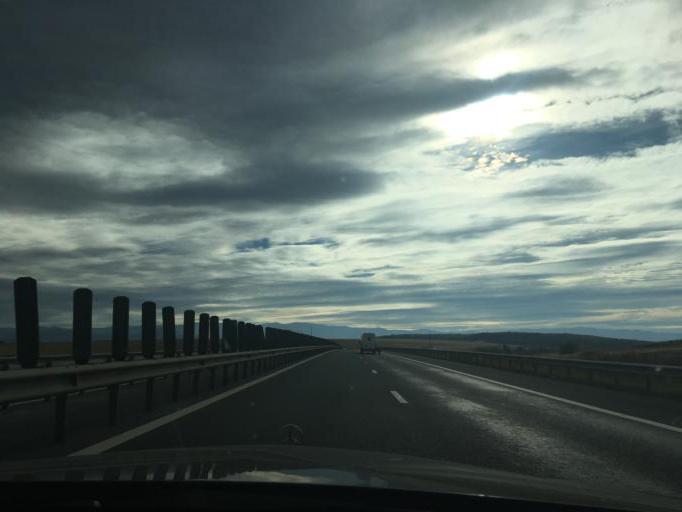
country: RO
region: Sibiu
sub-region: Comuna Sura Mica
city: Sura Mica
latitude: 45.8082
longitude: 24.0613
